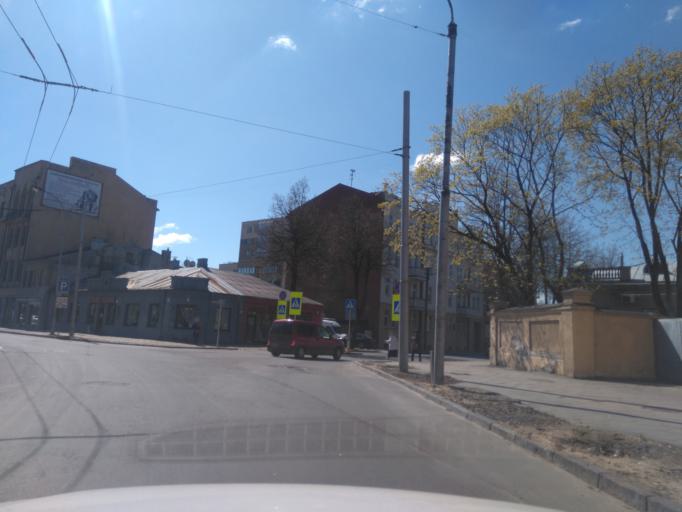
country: LT
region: Kauno apskritis
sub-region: Kaunas
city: Aleksotas
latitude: 54.8909
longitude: 23.9247
